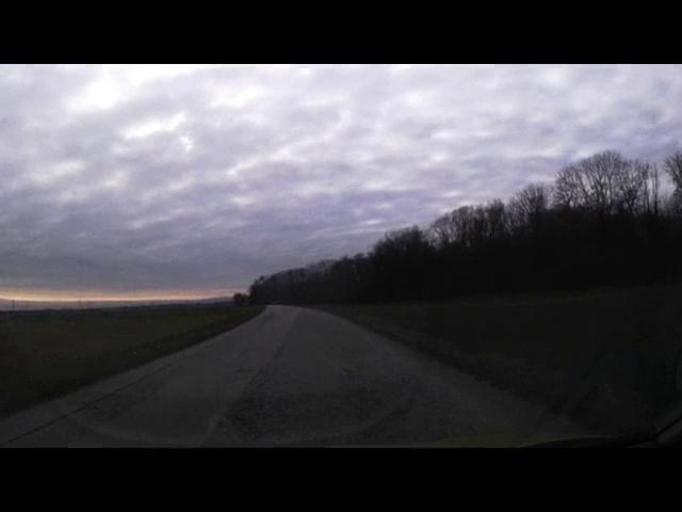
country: AT
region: Lower Austria
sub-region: Politischer Bezirk Wiener Neustadt
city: Ebenfurth
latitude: 47.8962
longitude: 16.3514
